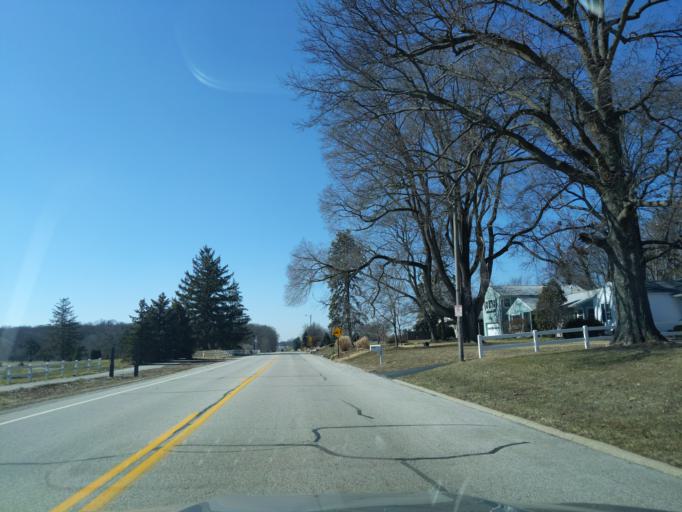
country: US
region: Indiana
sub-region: Tippecanoe County
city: West Lafayette
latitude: 40.4388
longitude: -86.9229
